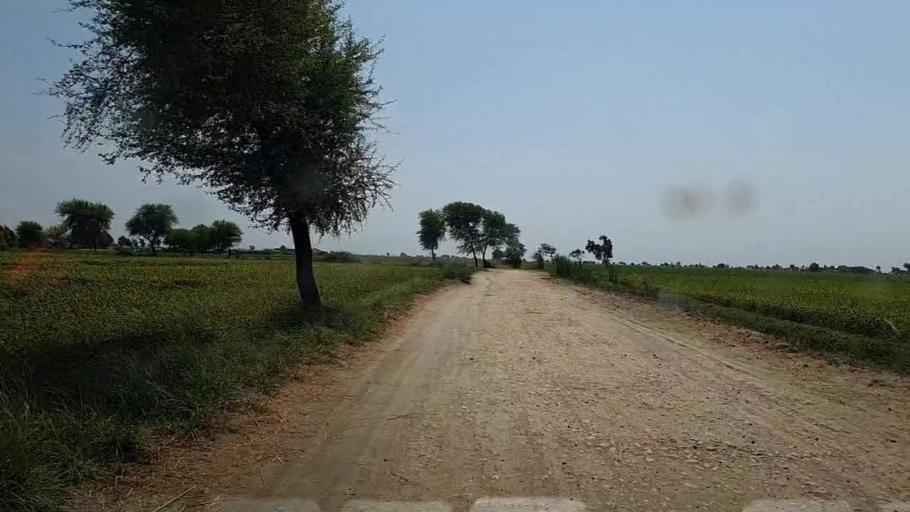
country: PK
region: Sindh
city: Kario
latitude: 24.6383
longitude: 68.4871
